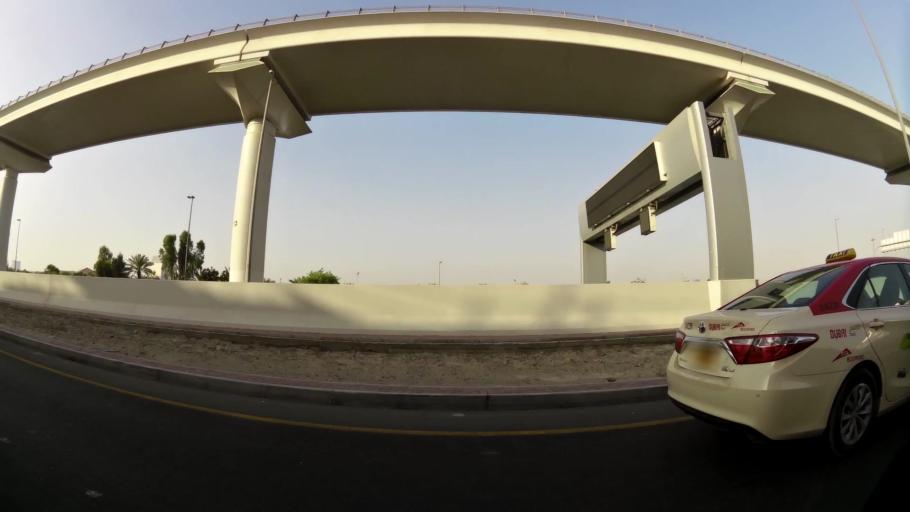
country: AE
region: Ash Shariqah
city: Sharjah
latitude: 25.2503
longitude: 55.3118
